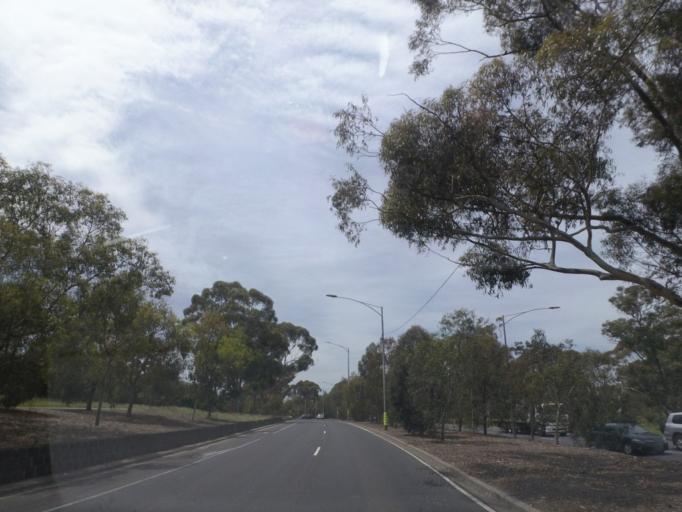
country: AU
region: Victoria
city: Parkville
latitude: -37.7892
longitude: 144.9473
